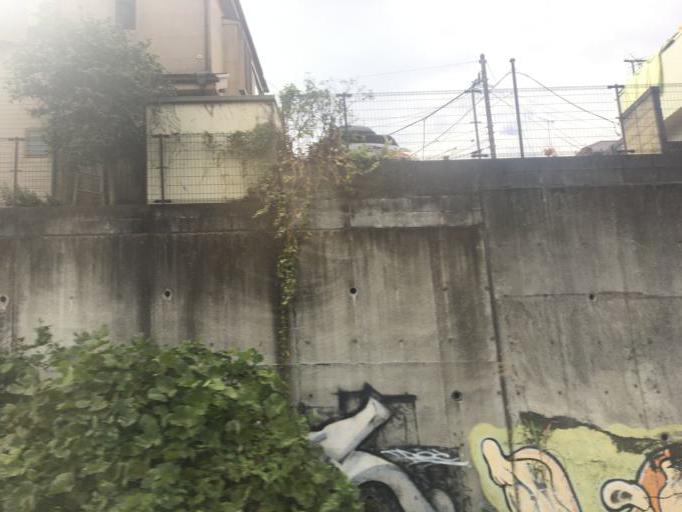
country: JP
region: Tokyo
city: Hino
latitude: 35.6891
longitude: 139.3648
